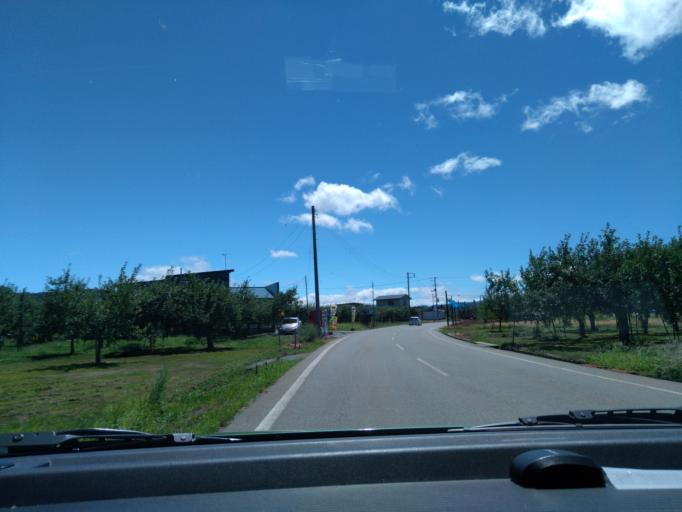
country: JP
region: Akita
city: Yuzawa
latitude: 39.2150
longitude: 140.5663
